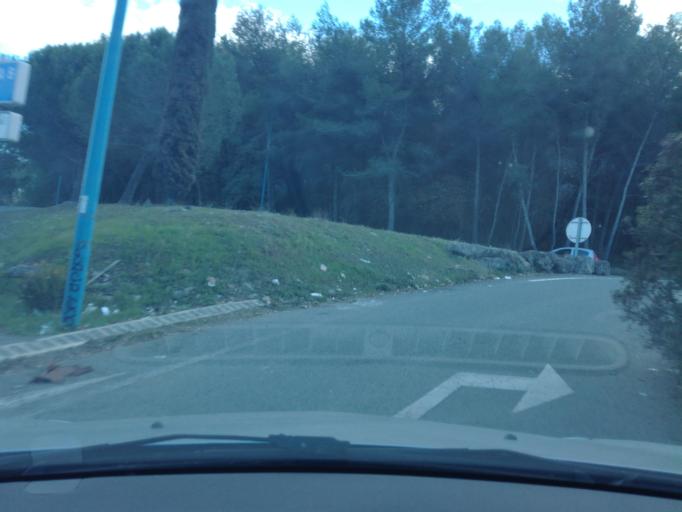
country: FR
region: Provence-Alpes-Cote d'Azur
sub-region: Departement des Alpes-Maritimes
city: Vallauris
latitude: 43.6020
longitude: 7.0726
